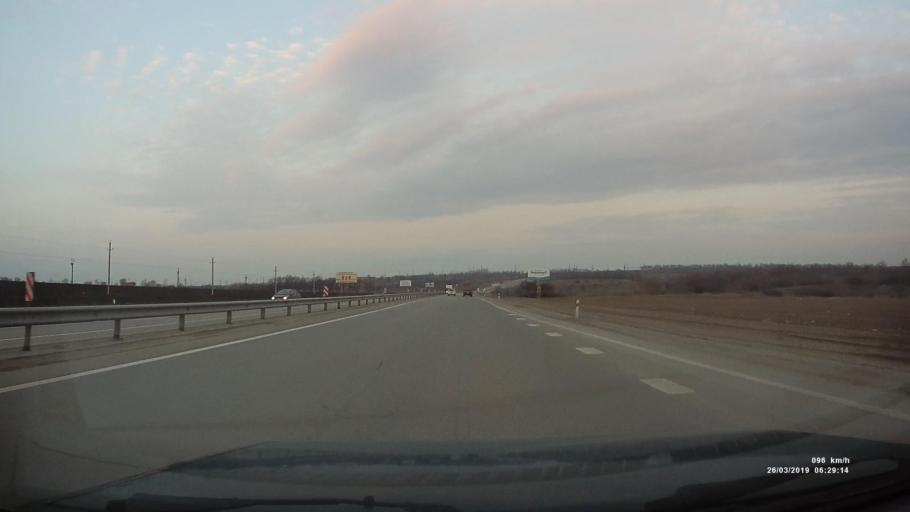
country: RU
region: Rostov
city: Kalinin
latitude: 47.2663
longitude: 39.5769
